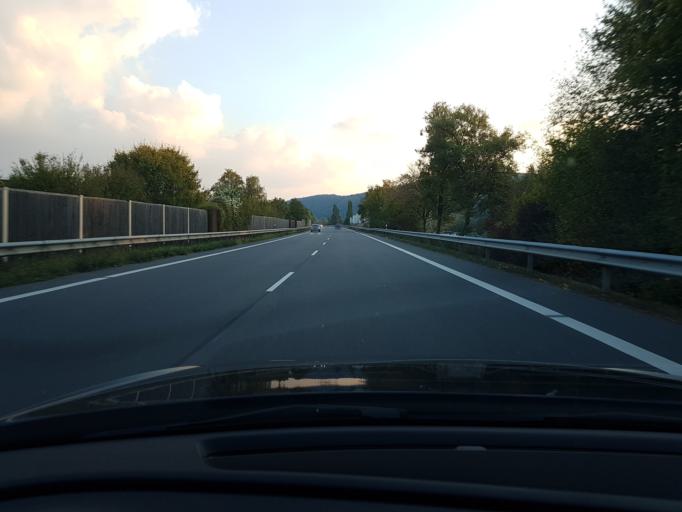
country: DE
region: Baden-Wuerttemberg
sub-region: Karlsruhe Region
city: Obrigheim
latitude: 49.3514
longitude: 9.1021
